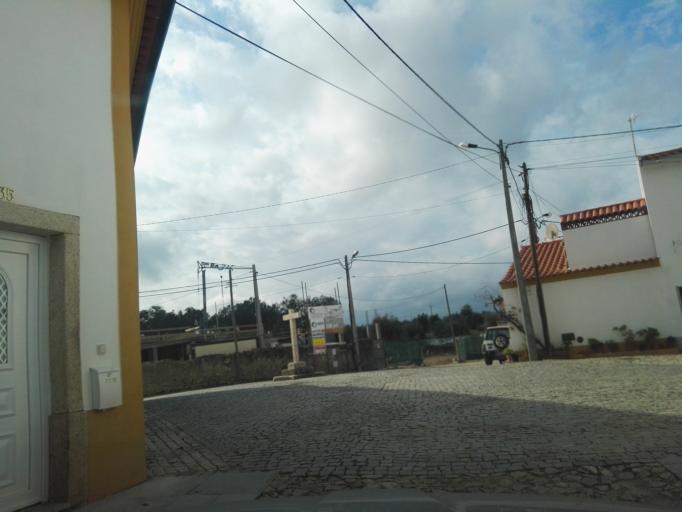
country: PT
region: Portalegre
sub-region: Nisa
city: Nisa
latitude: 39.4838
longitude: -7.7235
